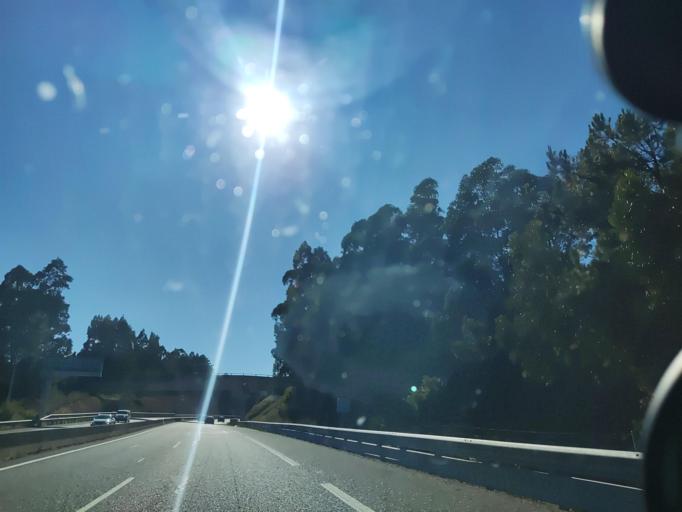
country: ES
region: Galicia
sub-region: Provincia da Coruna
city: Boiro
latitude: 42.6242
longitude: -8.9318
